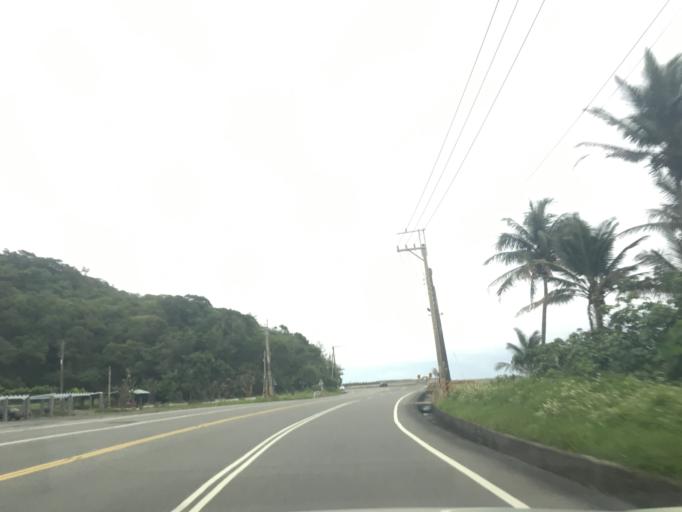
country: TW
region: Taiwan
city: Hengchun
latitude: 22.3309
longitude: 120.8925
